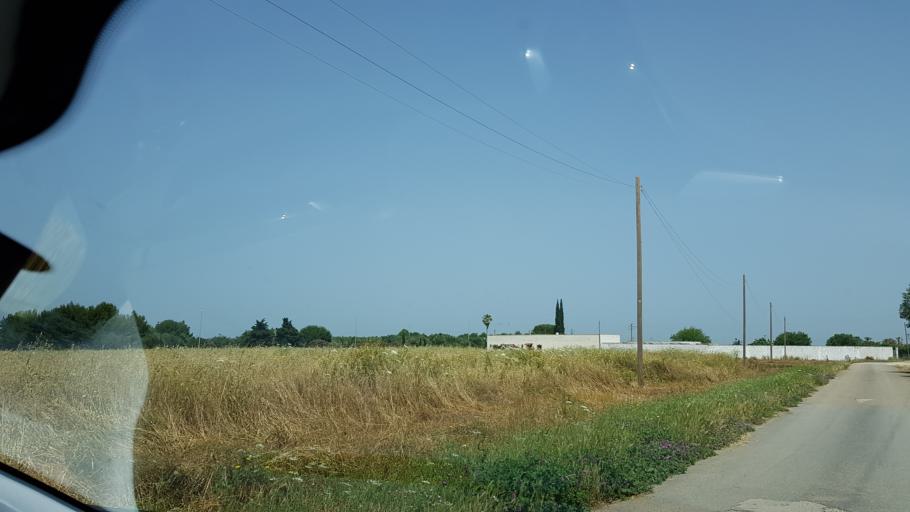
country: IT
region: Apulia
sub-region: Provincia di Brindisi
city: Mesagne
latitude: 40.5531
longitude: 17.8256
